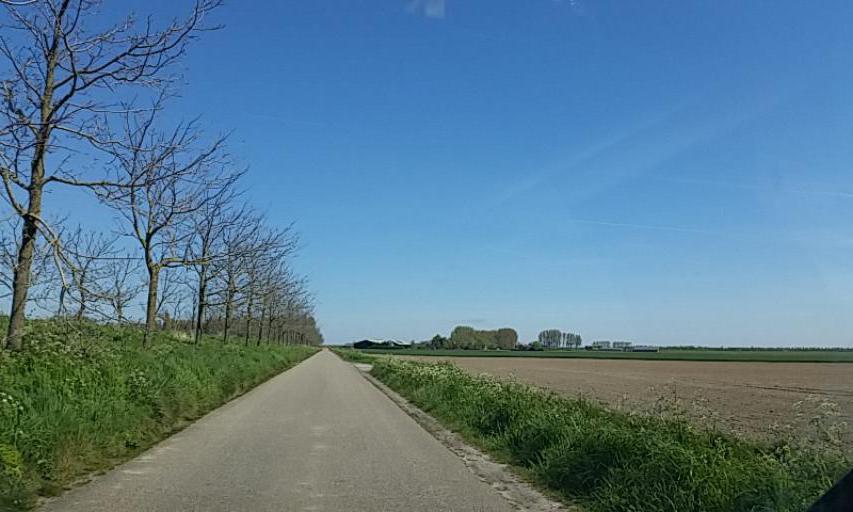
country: NL
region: Zeeland
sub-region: Gemeente Borsele
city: Borssele
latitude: 51.3357
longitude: 3.7107
